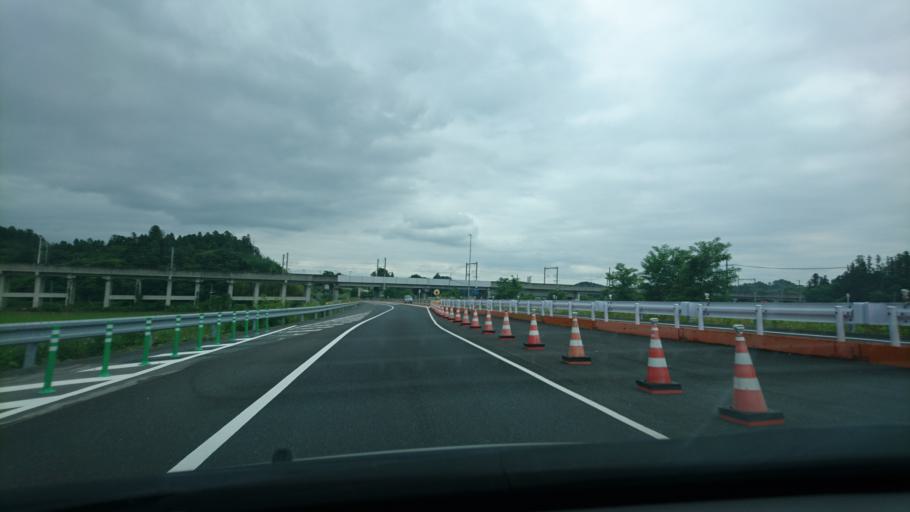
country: JP
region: Miyagi
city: Kogota
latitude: 38.7300
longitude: 141.0580
